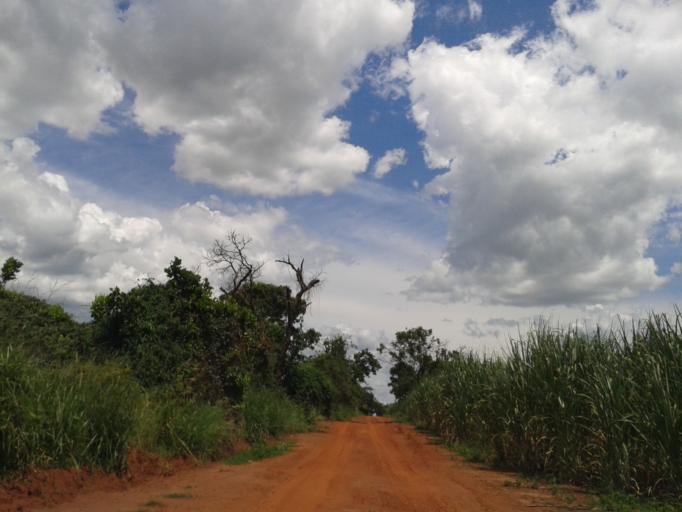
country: BR
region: Minas Gerais
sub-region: Ituiutaba
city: Ituiutaba
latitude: -18.8600
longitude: -49.4968
